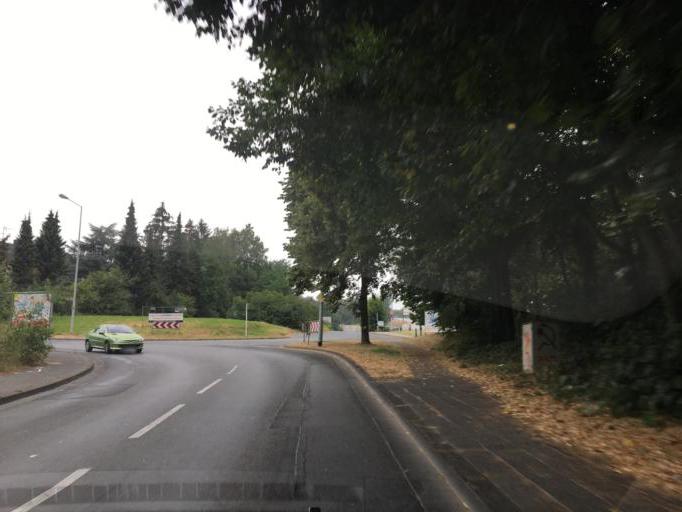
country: DE
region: North Rhine-Westphalia
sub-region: Regierungsbezirk Dusseldorf
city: Monchengladbach
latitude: 51.1337
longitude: 6.4404
